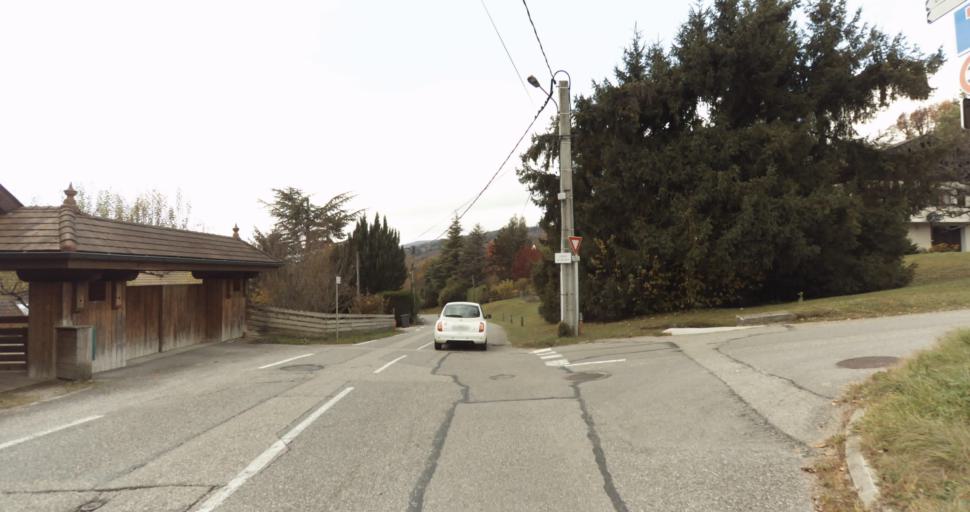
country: FR
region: Rhone-Alpes
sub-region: Departement de la Haute-Savoie
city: Pringy
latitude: 45.9577
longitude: 6.1162
